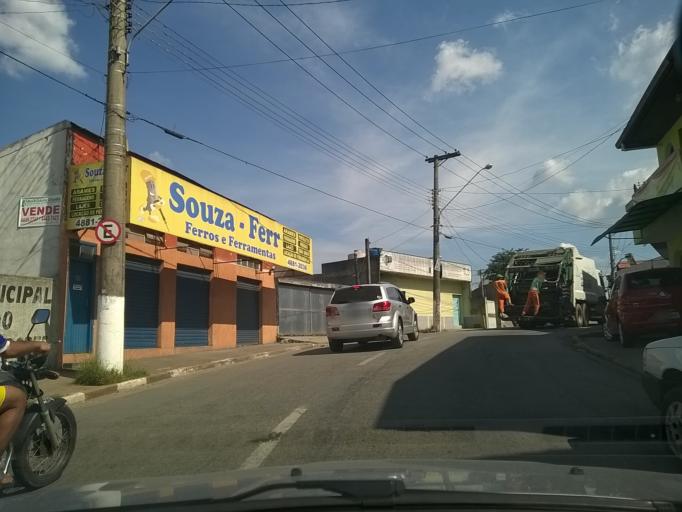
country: BR
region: Sao Paulo
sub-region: Francisco Morato
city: Francisco Morato
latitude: -23.2774
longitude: -46.7458
